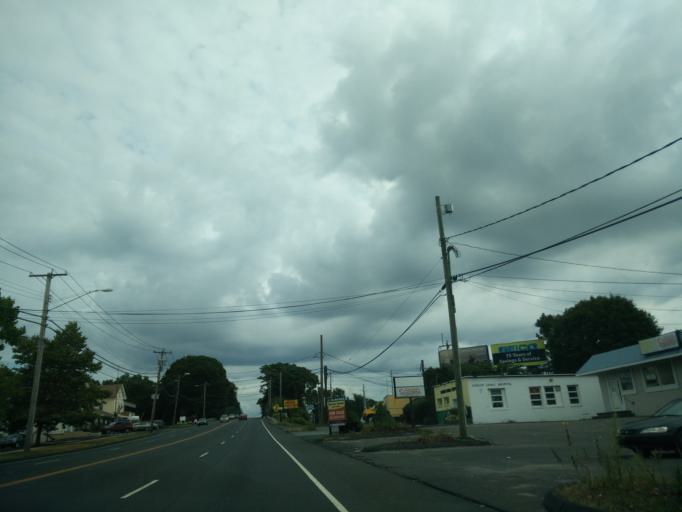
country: US
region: Connecticut
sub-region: Fairfield County
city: Stratford
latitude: 41.1988
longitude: -73.1282
